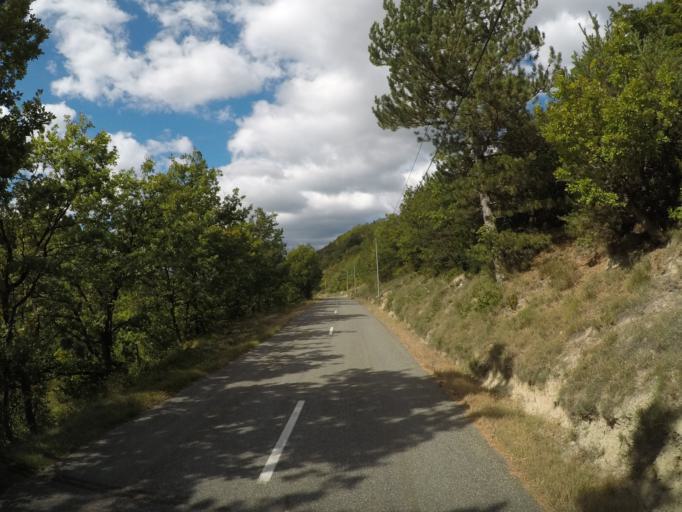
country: FR
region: Provence-Alpes-Cote d'Azur
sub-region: Departement des Hautes-Alpes
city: Laragne-Monteglin
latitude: 44.1740
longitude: 5.6949
